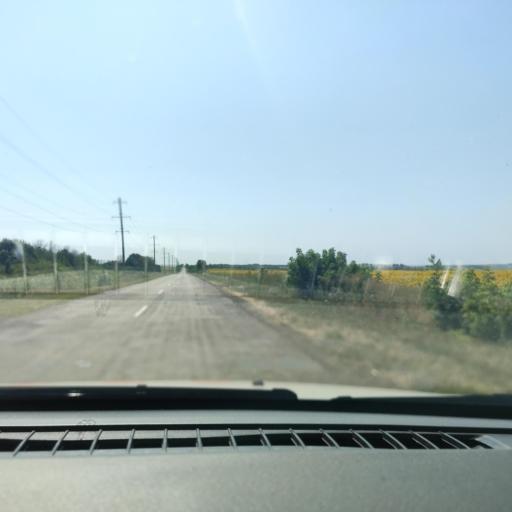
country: RU
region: Voronezj
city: Ol'khovatka
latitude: 50.6242
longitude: 39.3209
